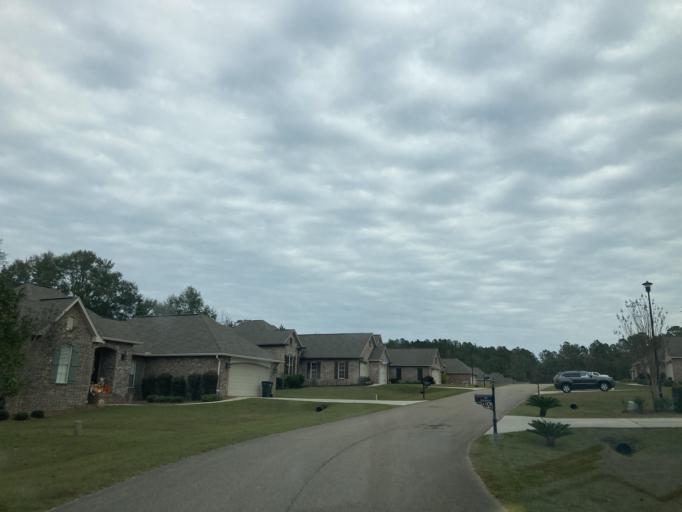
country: US
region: Mississippi
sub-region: Lamar County
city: West Hattiesburg
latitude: 31.2925
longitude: -89.4447
